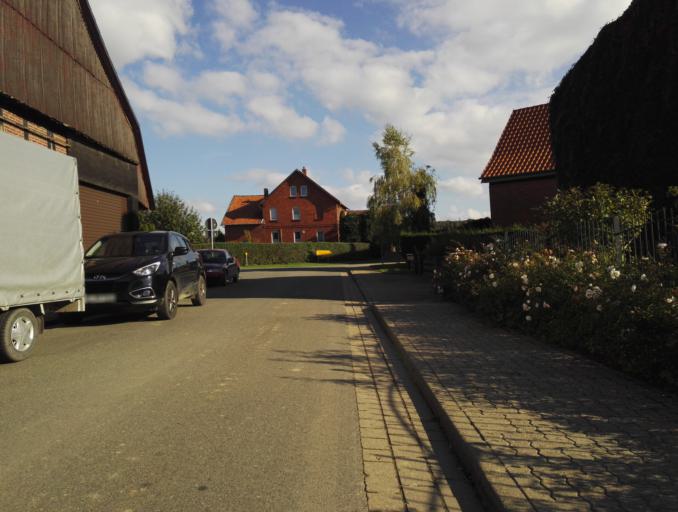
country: DE
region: Lower Saxony
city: Schellerten
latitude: 52.1436
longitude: 10.1321
